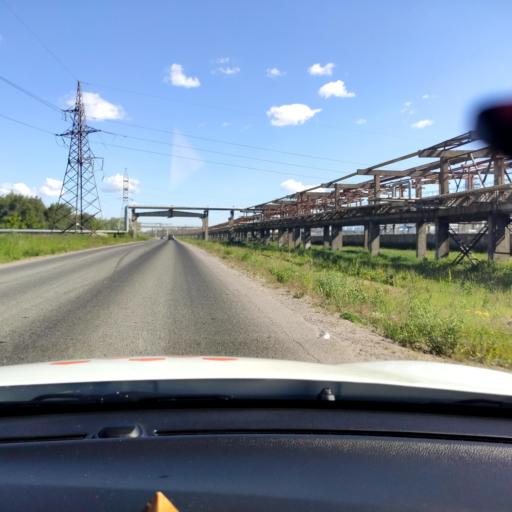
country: RU
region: Tatarstan
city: Staroye Arakchino
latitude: 55.8754
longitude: 48.9750
